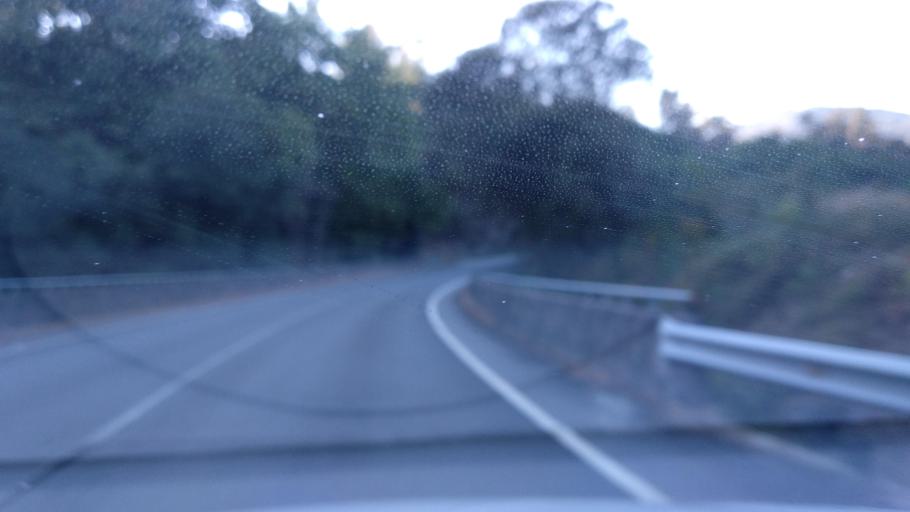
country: ES
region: Galicia
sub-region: Provincia de Pontevedra
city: Ponte Caldelas
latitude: 42.3403
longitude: -8.5566
